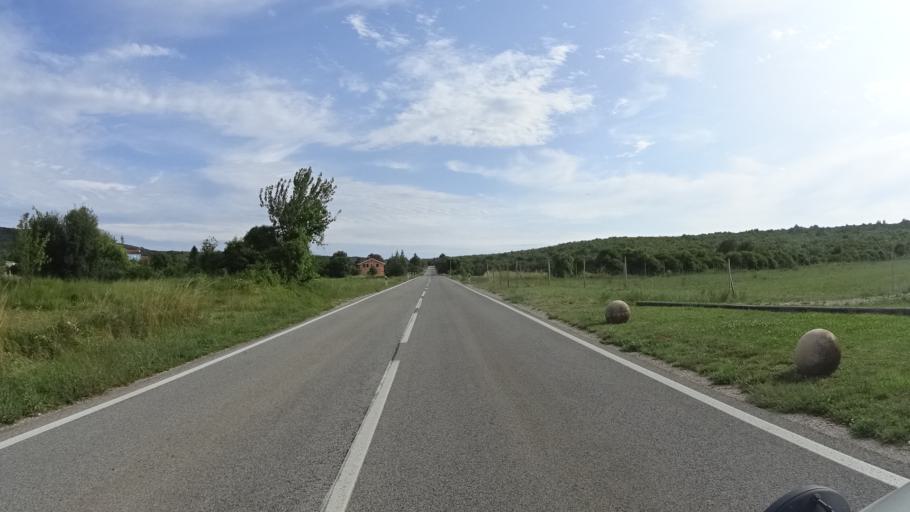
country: HR
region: Istarska
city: Rasa
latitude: 45.0715
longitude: 14.0939
